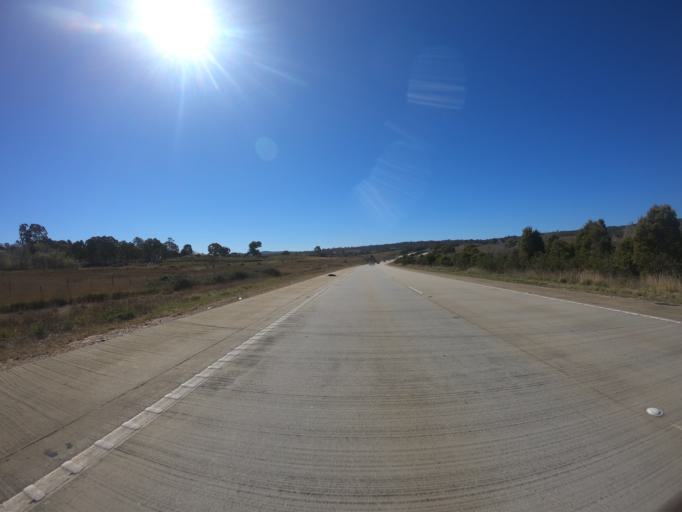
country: AU
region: New South Wales
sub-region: Yass Valley
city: Gundaroo
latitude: -35.1222
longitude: 149.3450
